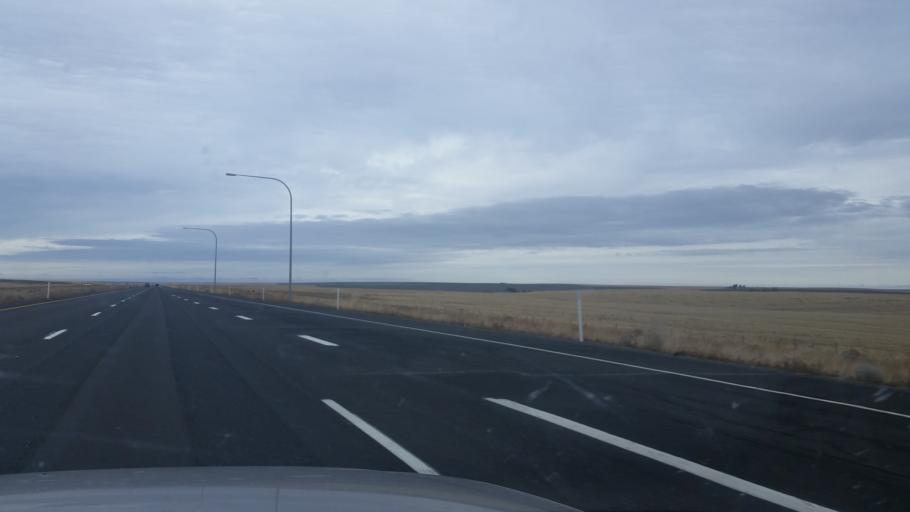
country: US
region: Washington
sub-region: Adams County
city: Ritzville
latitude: 47.1112
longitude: -118.5010
